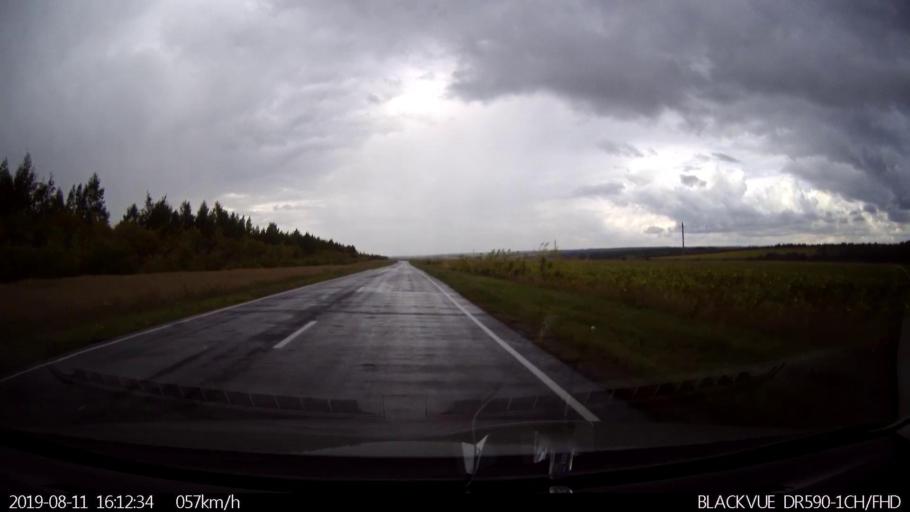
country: RU
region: Ulyanovsk
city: Ignatovka
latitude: 54.0125
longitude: 47.6400
